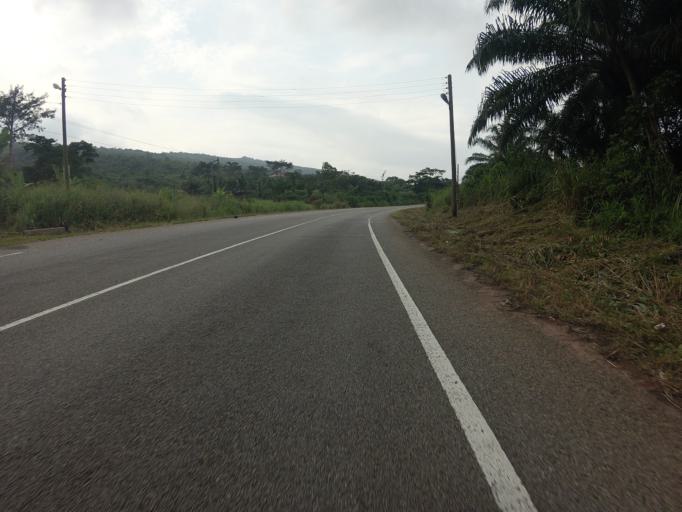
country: GH
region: Volta
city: Ho
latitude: 6.6517
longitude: 0.4695
